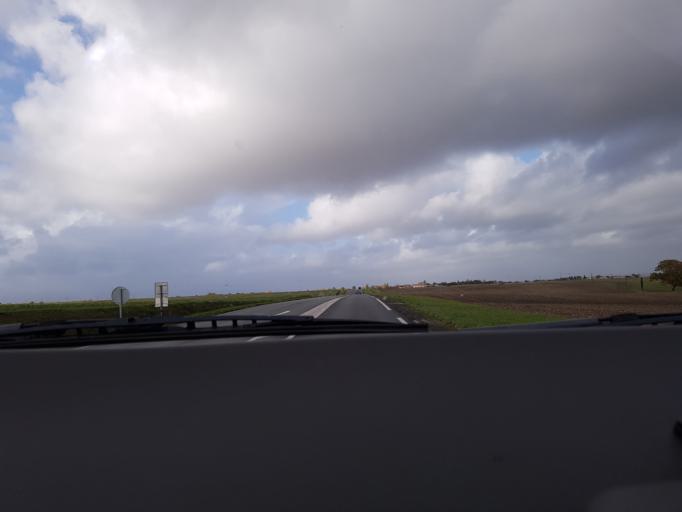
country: FR
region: Poitou-Charentes
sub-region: Departement de la Charente-Maritime
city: Pons
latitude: 45.6424
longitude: -0.5809
